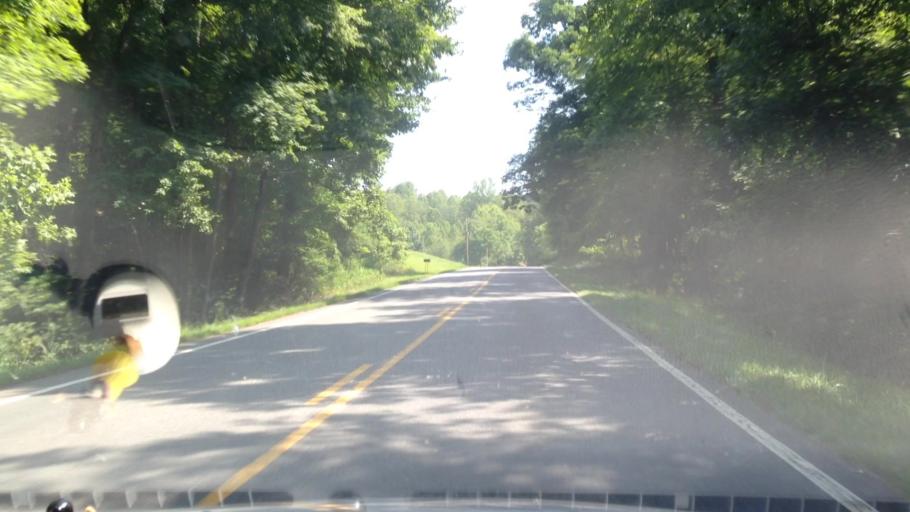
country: US
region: North Carolina
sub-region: Surry County
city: Flat Rock
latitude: 36.5654
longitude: -80.4633
